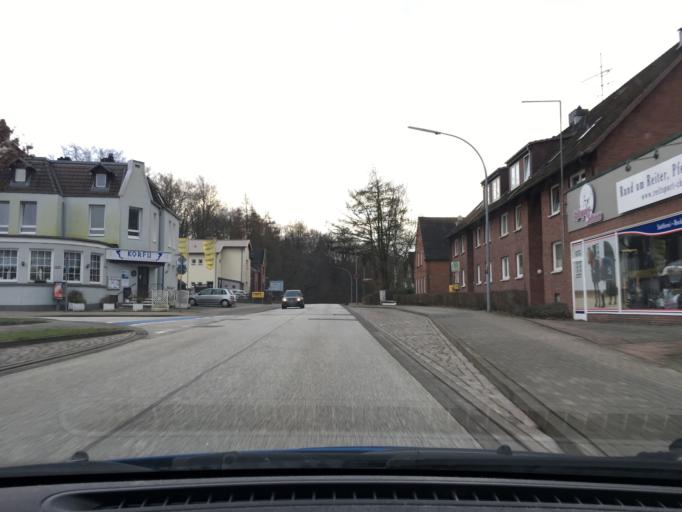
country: DE
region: Schleswig-Holstein
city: Heiligenstedten
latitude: 53.9439
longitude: 9.4960
